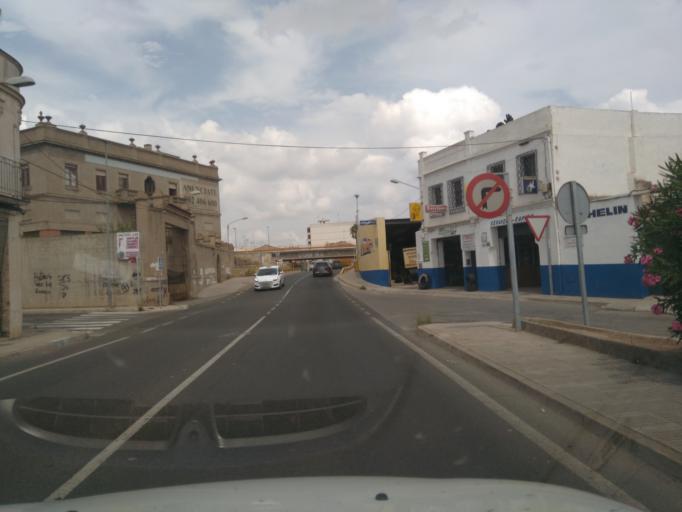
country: ES
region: Valencia
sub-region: Provincia de Valencia
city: Alzira
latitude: 39.1436
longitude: -0.4380
